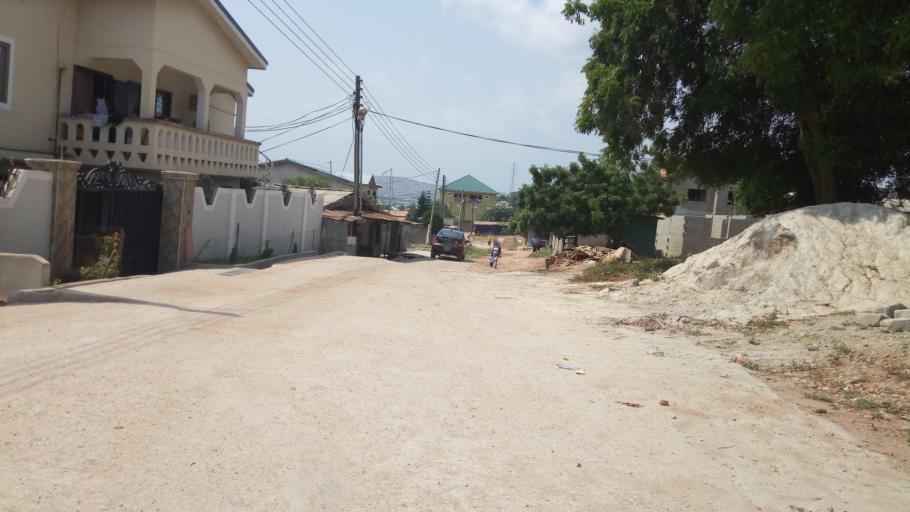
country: GH
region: Greater Accra
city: Gbawe
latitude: 5.5627
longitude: -0.3079
